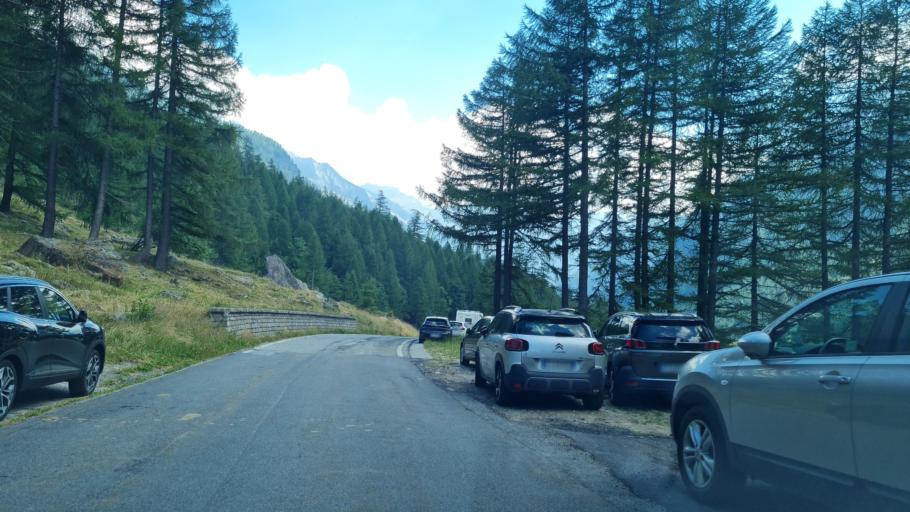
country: IT
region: Piedmont
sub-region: Provincia Verbano-Cusio-Ossola
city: Formazza
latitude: 46.3991
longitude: 8.4198
